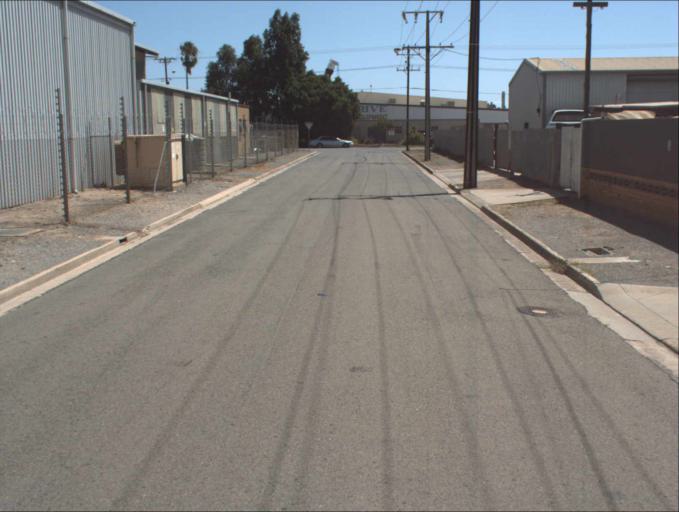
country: AU
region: South Australia
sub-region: Charles Sturt
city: Woodville North
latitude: -34.8448
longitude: 138.5518
